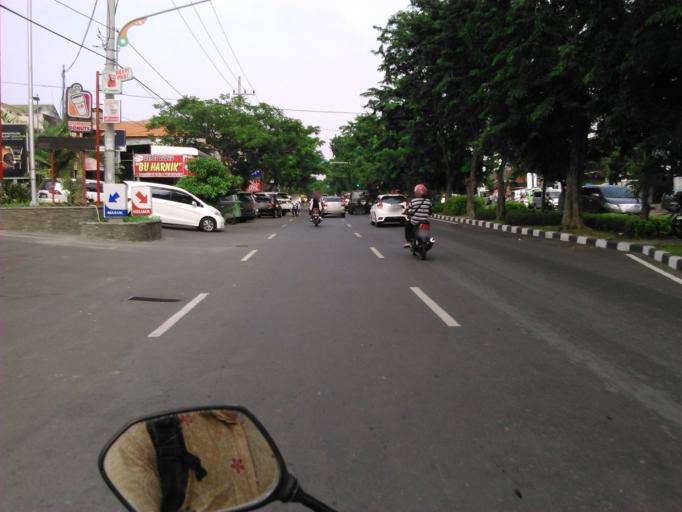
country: ID
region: East Java
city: Brongkalan
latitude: -7.2666
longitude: 112.7684
